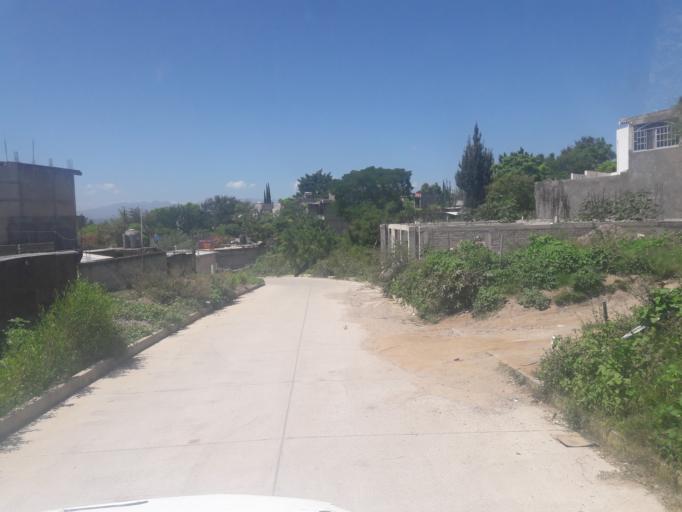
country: MX
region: Oaxaca
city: Ciudad de Huajuapam de Leon
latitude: 17.8046
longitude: -97.8021
